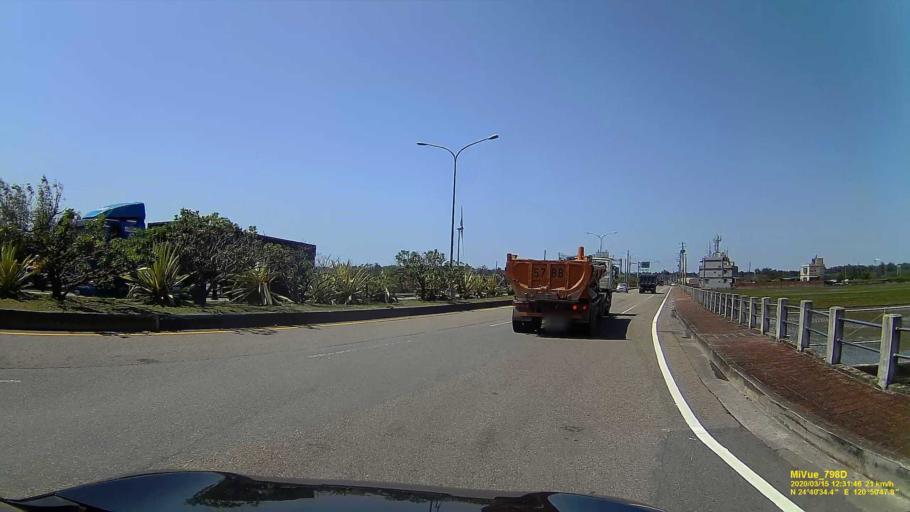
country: TW
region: Taiwan
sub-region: Miaoli
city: Miaoli
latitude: 24.6762
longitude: 120.8463
